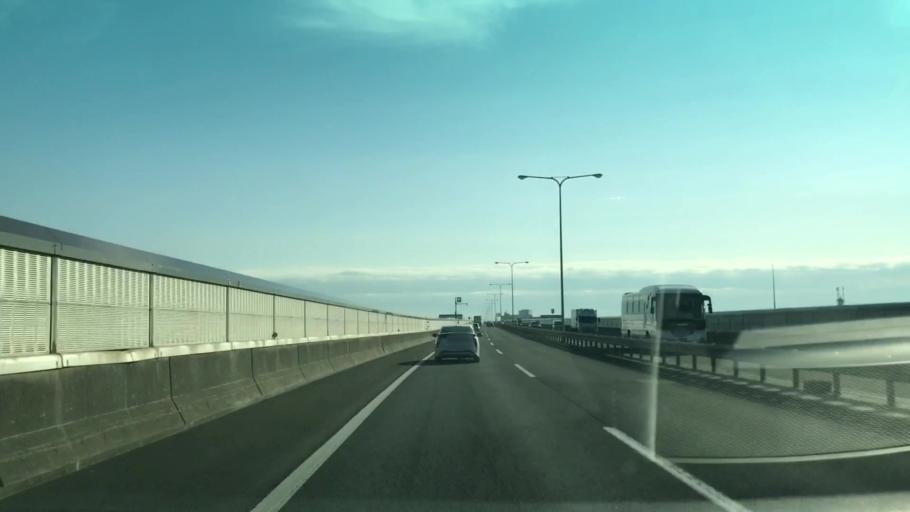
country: JP
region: Hokkaido
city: Sapporo
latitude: 43.1031
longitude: 141.3796
